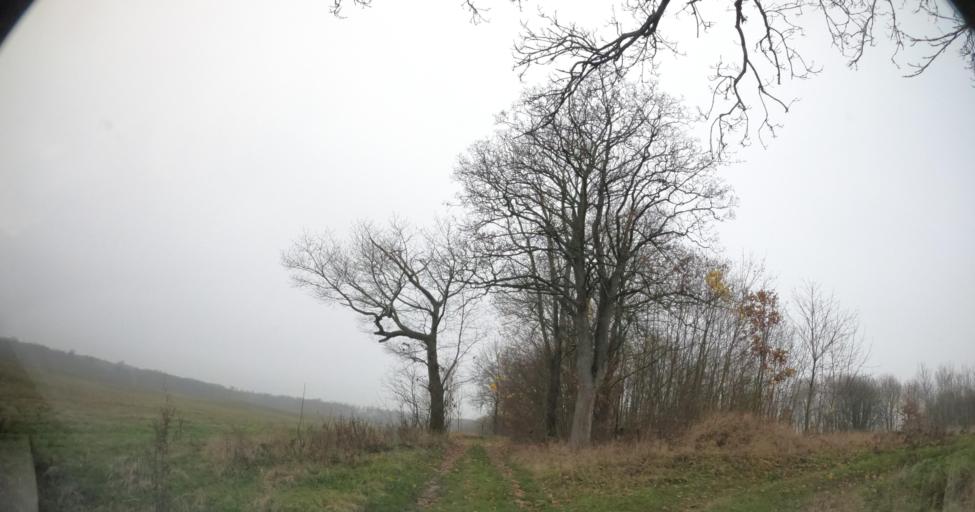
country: PL
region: West Pomeranian Voivodeship
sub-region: Powiat drawski
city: Drawsko Pomorskie
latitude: 53.5939
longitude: 15.7866
